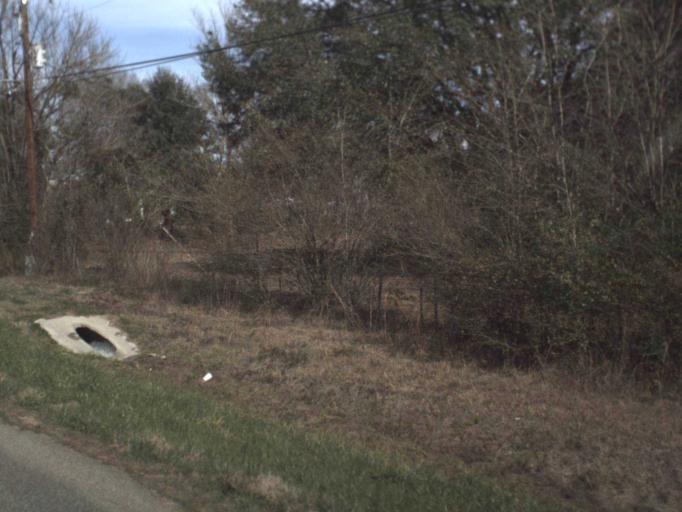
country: US
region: Florida
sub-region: Washington County
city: Chipley
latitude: 30.8622
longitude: -85.5275
